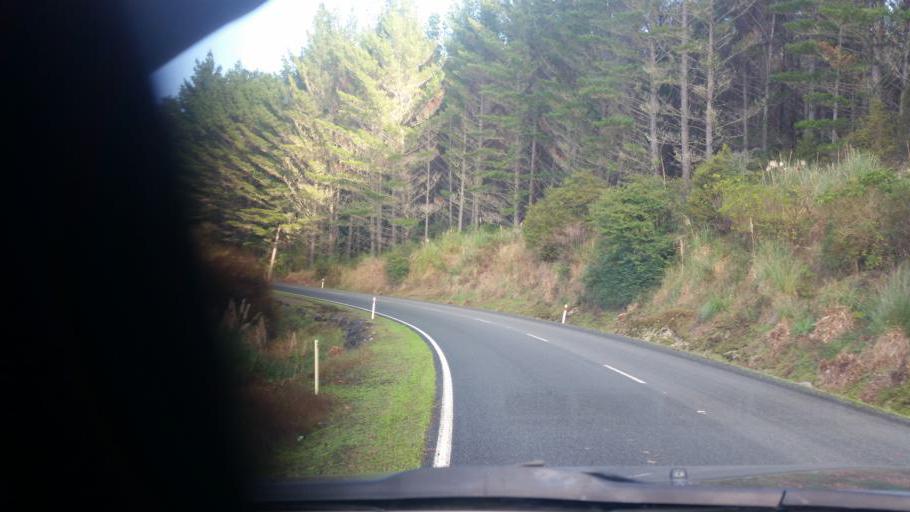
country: NZ
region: Auckland
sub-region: Auckland
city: Wellsford
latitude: -36.2168
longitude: 174.4665
